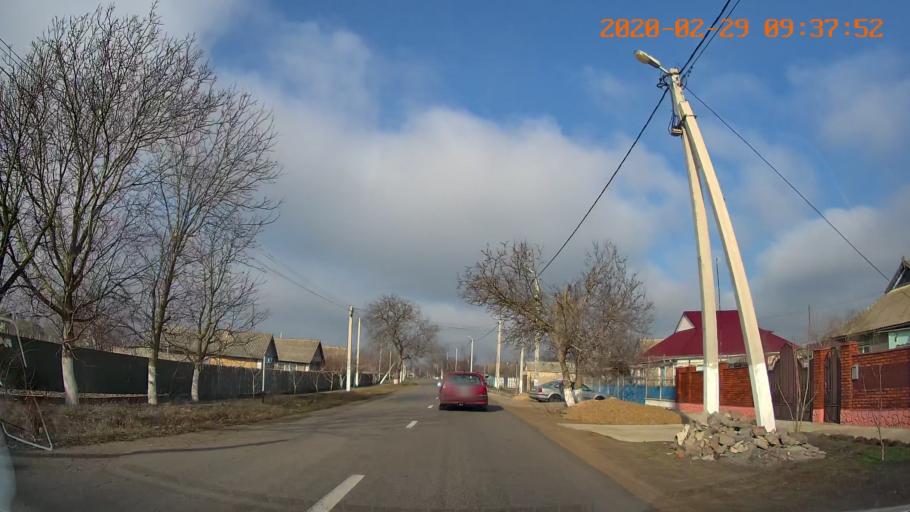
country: MD
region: Telenesti
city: Dnestrovsc
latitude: 46.6290
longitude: 29.8728
